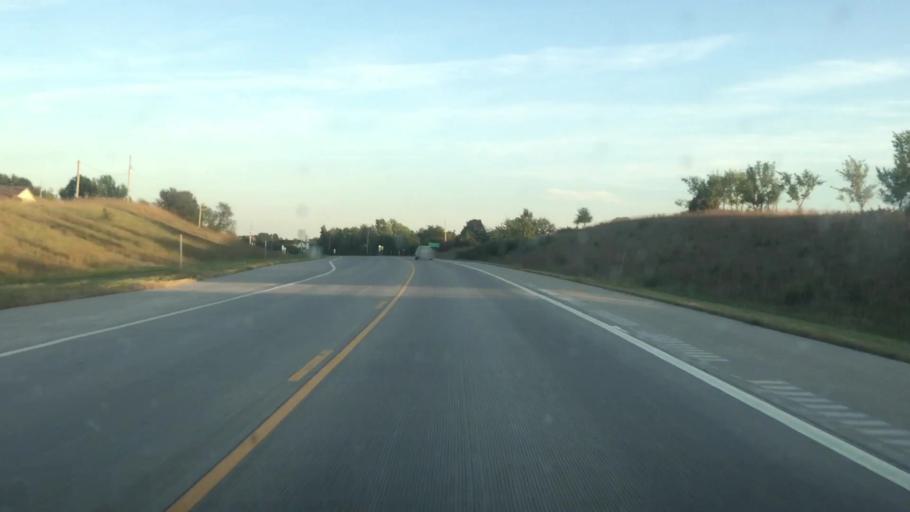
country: US
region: Kansas
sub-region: Leavenworth County
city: Leavenworth
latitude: 39.3706
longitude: -95.0519
